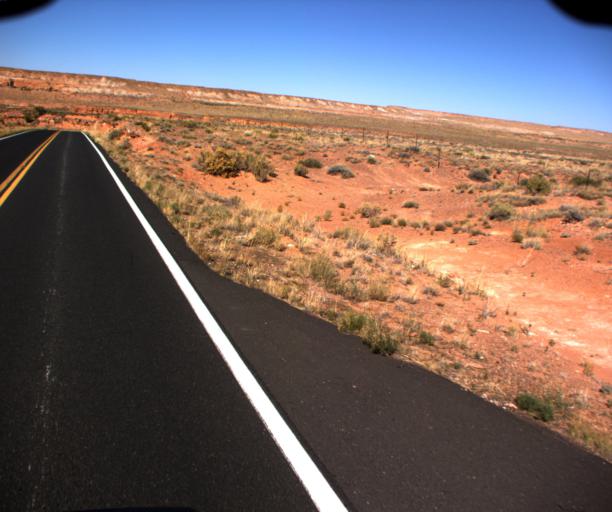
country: US
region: Arizona
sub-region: Coconino County
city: Tuba City
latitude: 36.0977
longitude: -111.1945
